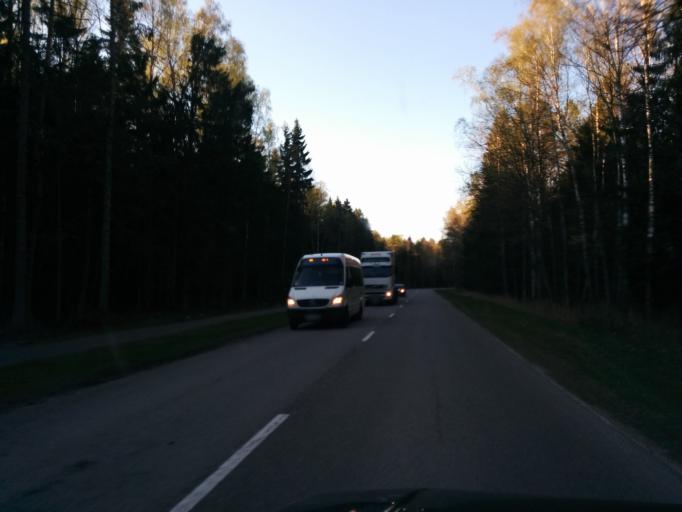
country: LV
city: Tireli
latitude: 56.9582
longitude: 23.5229
